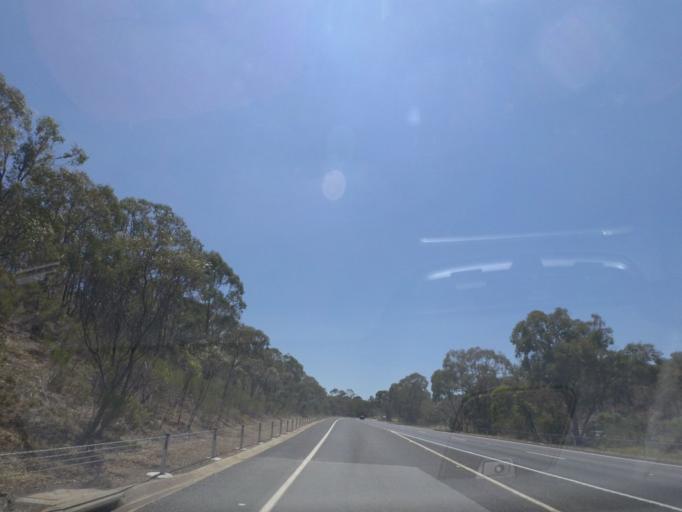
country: AU
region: Victoria
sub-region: Murrindindi
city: Kinglake West
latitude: -36.9615
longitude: 145.1837
